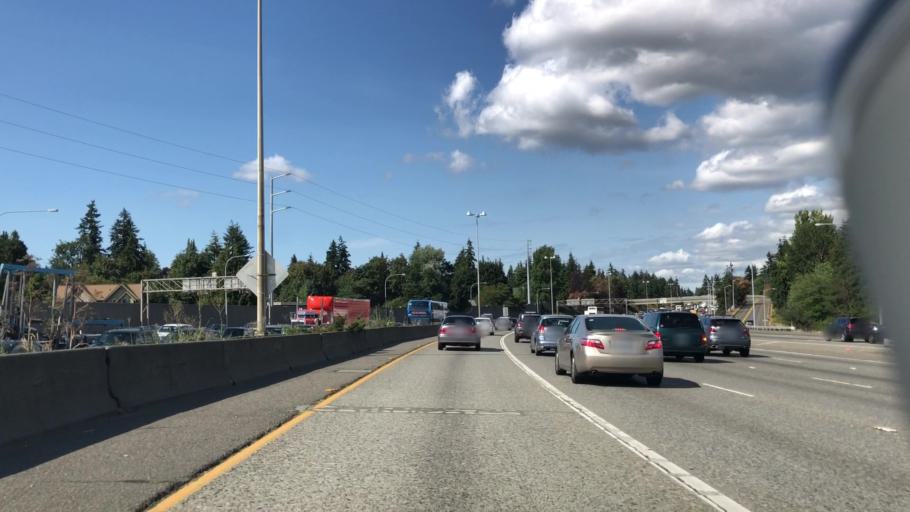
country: US
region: Washington
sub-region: King County
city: Shoreline
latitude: 47.7100
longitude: -122.3317
